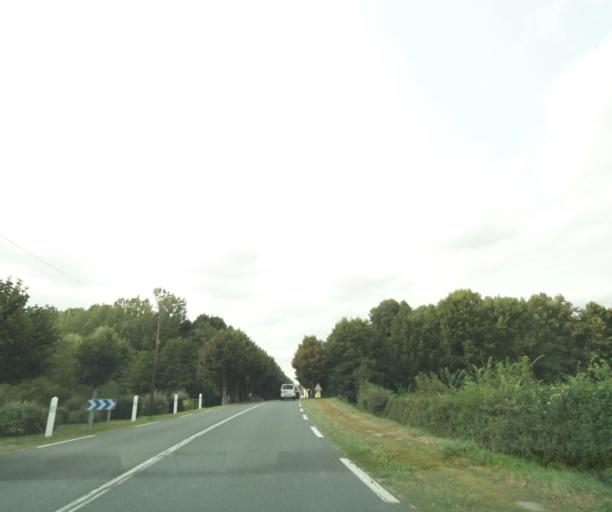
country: FR
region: Centre
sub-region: Departement de l'Indre
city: Chatillon-sur-Indre
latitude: 47.0174
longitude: 1.1104
